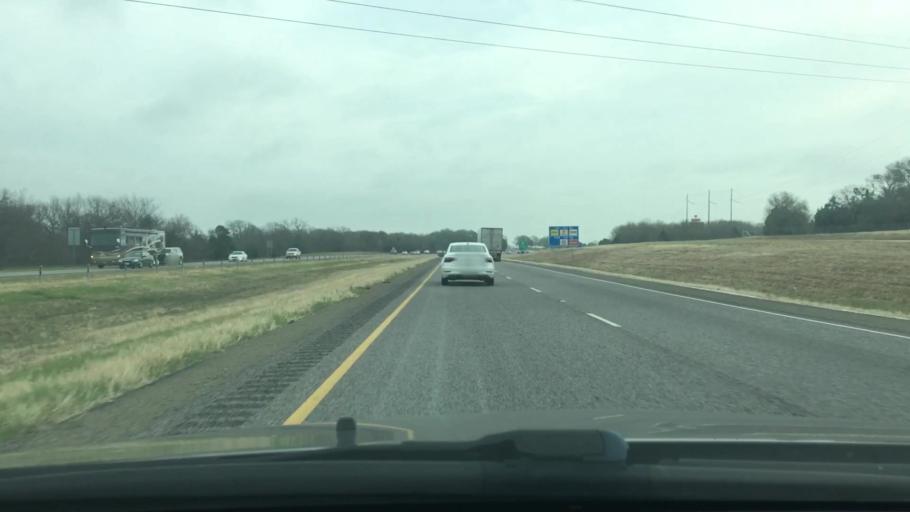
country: US
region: Texas
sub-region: Freestone County
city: Fairfield
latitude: 31.7354
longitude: -96.1856
